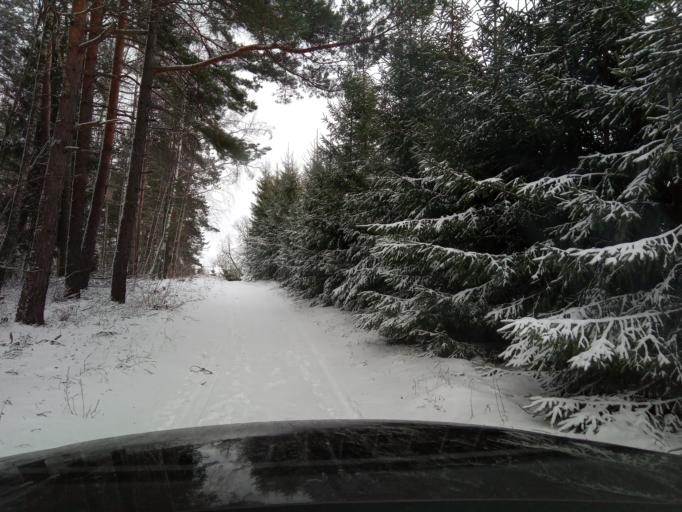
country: LT
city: Zarasai
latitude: 55.6757
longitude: 26.0284
